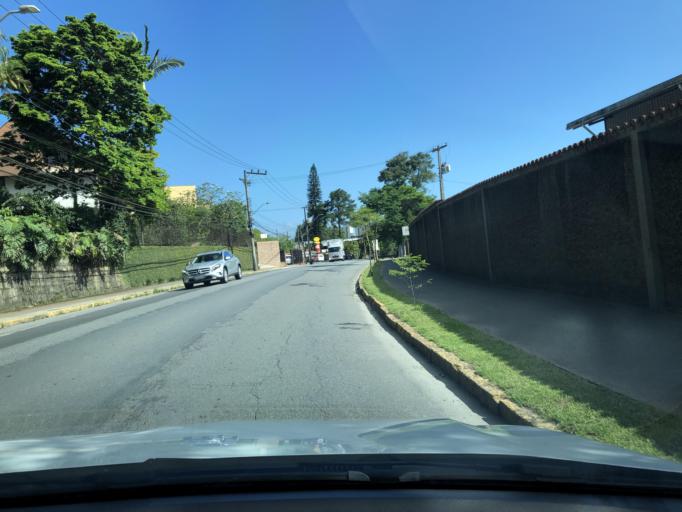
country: BR
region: Santa Catarina
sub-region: Joinville
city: Joinville
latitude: -26.3051
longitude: -48.8380
